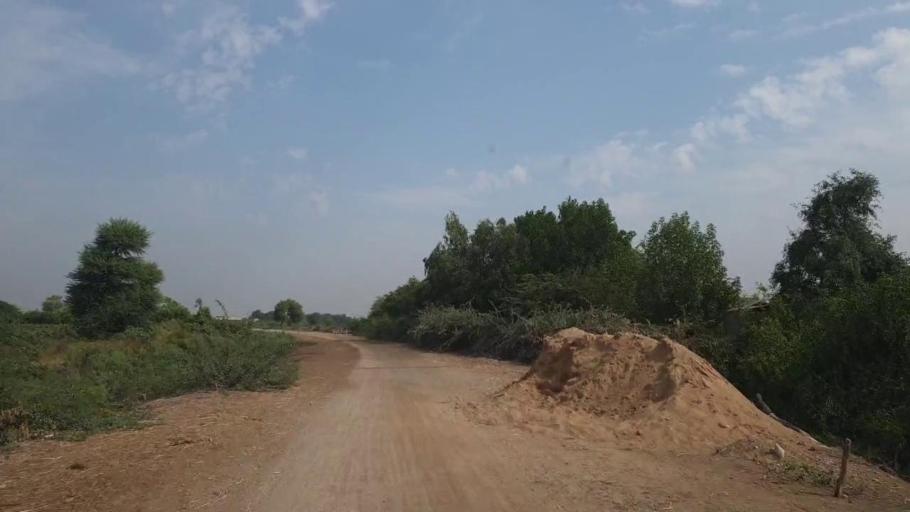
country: PK
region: Sindh
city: Rajo Khanani
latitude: 24.9637
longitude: 68.9913
